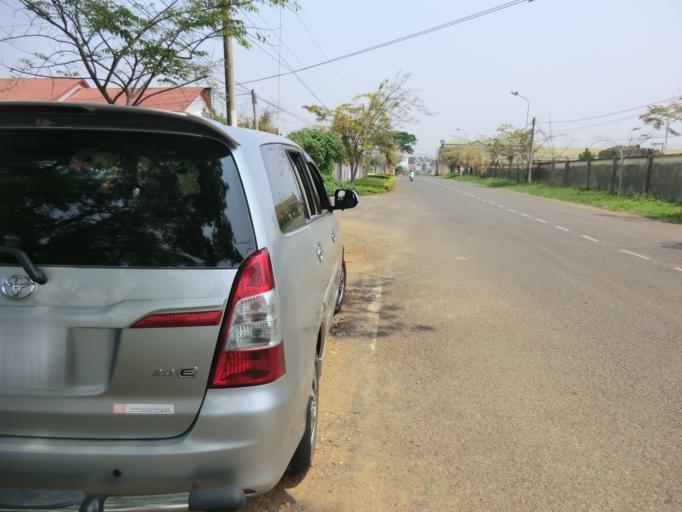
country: VN
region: Lam Dong
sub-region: Thanh Pho Bao Loc
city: Bao Loc
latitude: 11.5467
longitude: 107.7981
